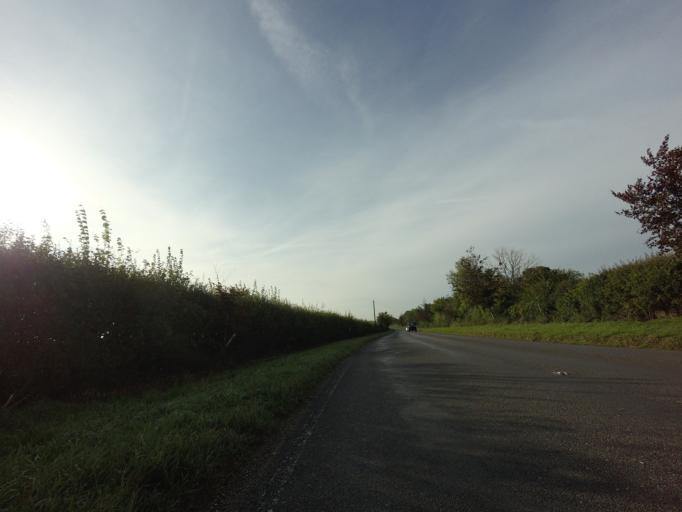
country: GB
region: England
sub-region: Cambridgeshire
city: Harston
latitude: 52.1326
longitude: 0.1011
